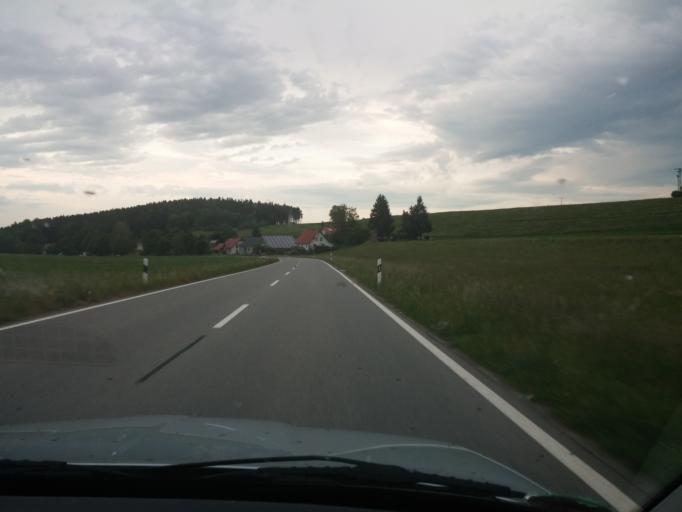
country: DE
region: Bavaria
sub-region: Swabia
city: Lautrach
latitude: 47.8851
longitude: 10.1221
